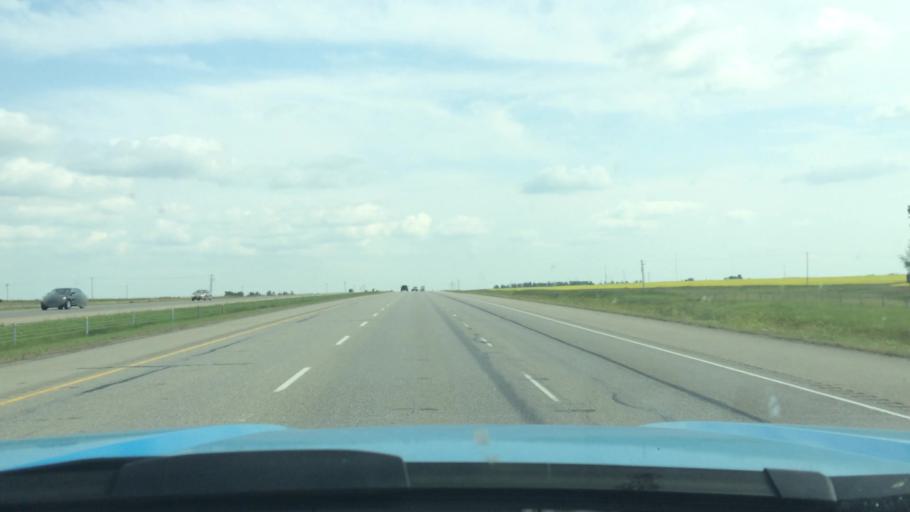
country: CA
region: Alberta
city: Crossfield
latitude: 51.4480
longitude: -114.0133
